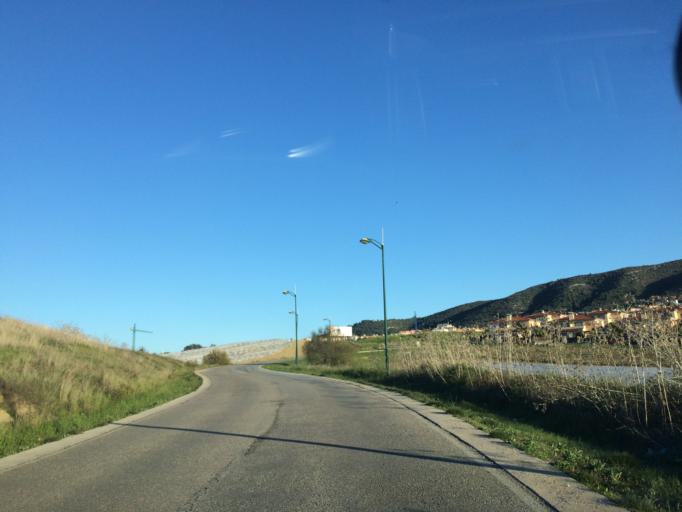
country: ES
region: Andalusia
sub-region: Provincia de Malaga
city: Alhaurin de la Torre
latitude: 36.6689
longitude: -4.5374
